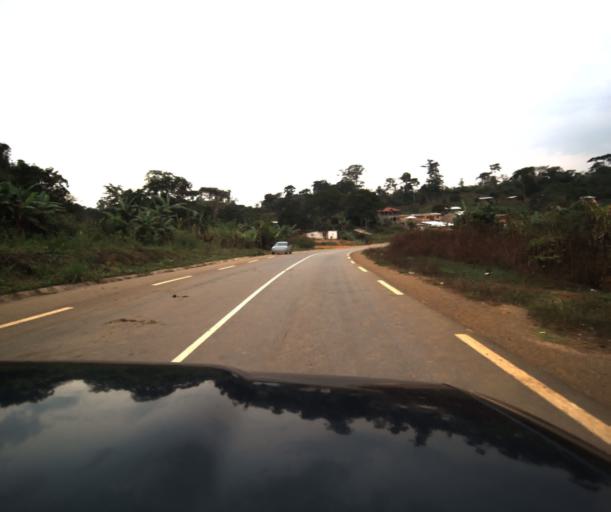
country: CM
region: Centre
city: Mbankomo
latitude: 3.7675
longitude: 11.4065
